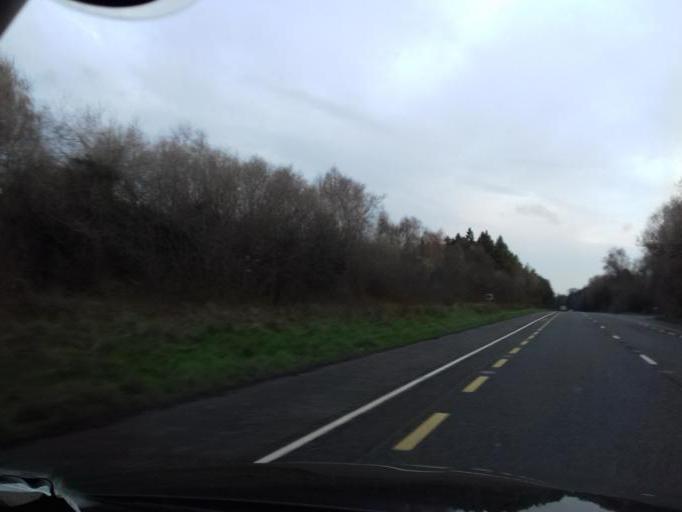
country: IE
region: Leinster
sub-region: Laois
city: Abbeyleix
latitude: 52.8917
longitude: -7.3631
